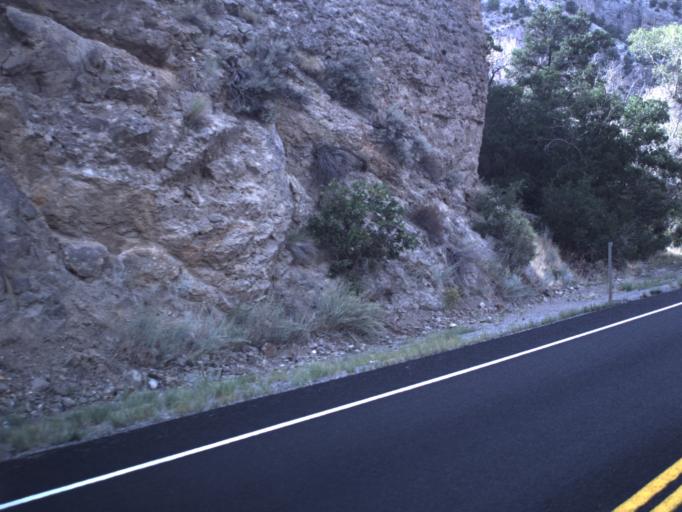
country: US
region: Utah
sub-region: Sevier County
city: Monroe
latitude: 38.5591
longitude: -112.2722
